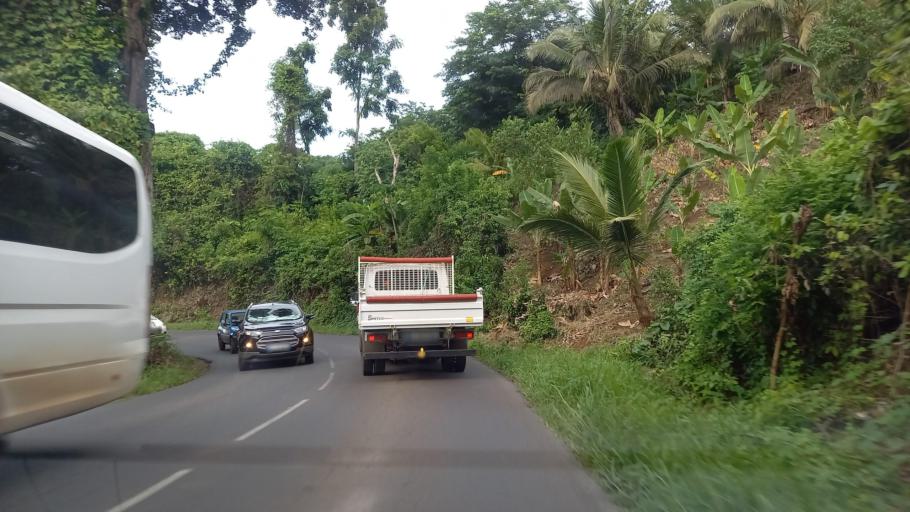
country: YT
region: Bandraboua
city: Bandraboua
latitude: -12.7400
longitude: 45.1179
